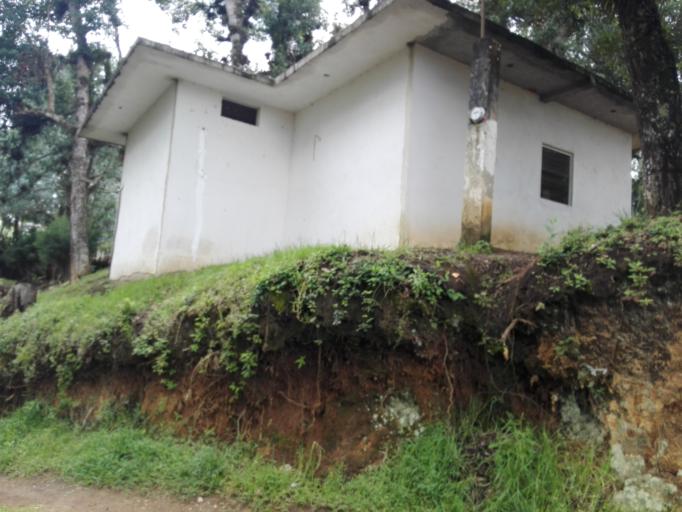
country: GT
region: Guatemala
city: Santa Catarina Pinula
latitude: 14.5311
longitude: -90.4953
